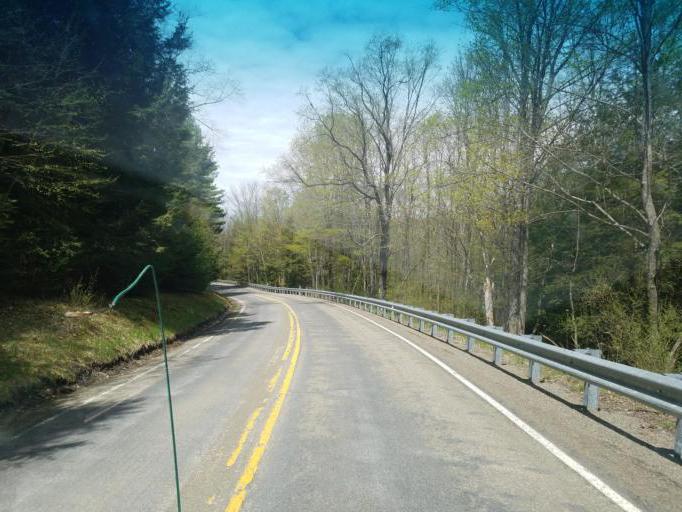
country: US
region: Pennsylvania
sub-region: Tioga County
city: Wellsboro
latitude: 41.7006
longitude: -77.4413
